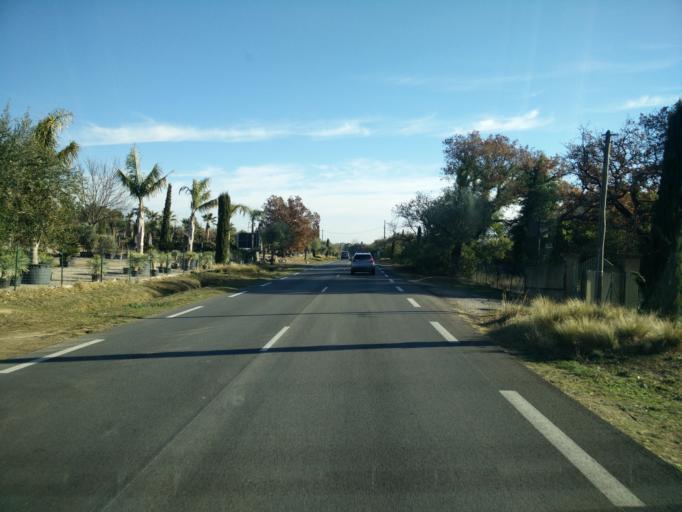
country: FR
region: Provence-Alpes-Cote d'Azur
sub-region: Departement du Var
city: Grimaud
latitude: 43.2690
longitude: 6.5364
